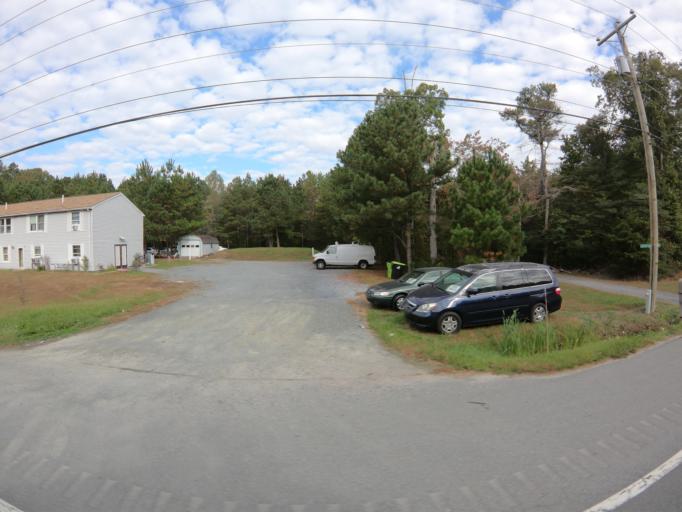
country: US
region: Delaware
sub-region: Sussex County
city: Georgetown
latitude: 38.7109
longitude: -75.3269
